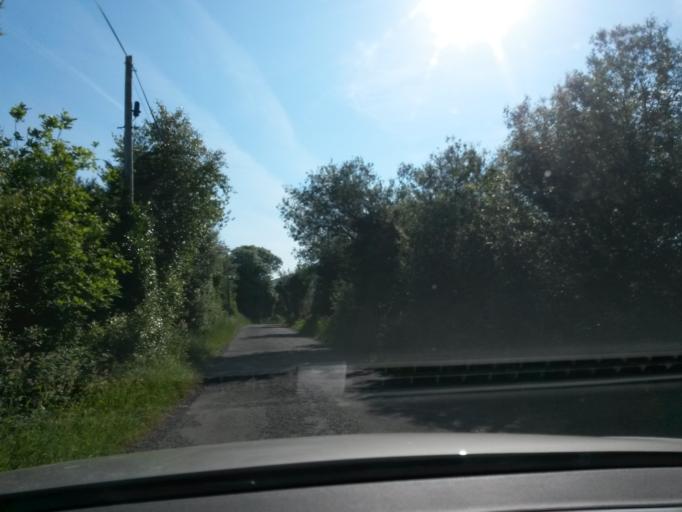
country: IE
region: Munster
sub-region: Ciarrai
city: Kenmare
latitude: 51.7833
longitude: -9.8111
